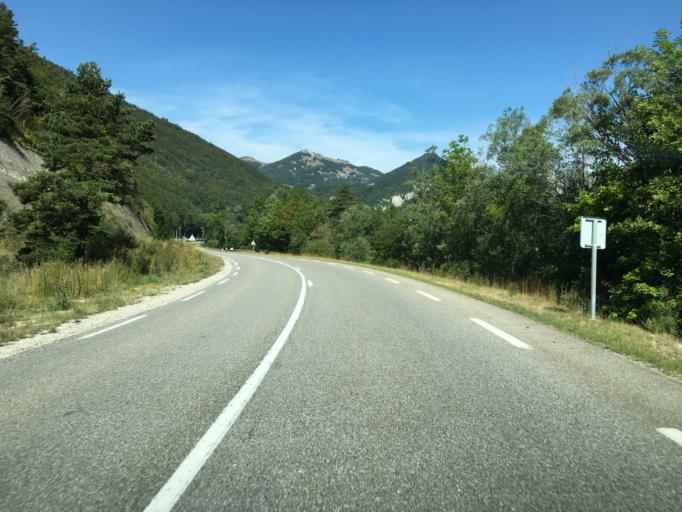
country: FR
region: Provence-Alpes-Cote d'Azur
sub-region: Departement des Hautes-Alpes
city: Veynes
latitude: 44.6482
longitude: 5.7020
